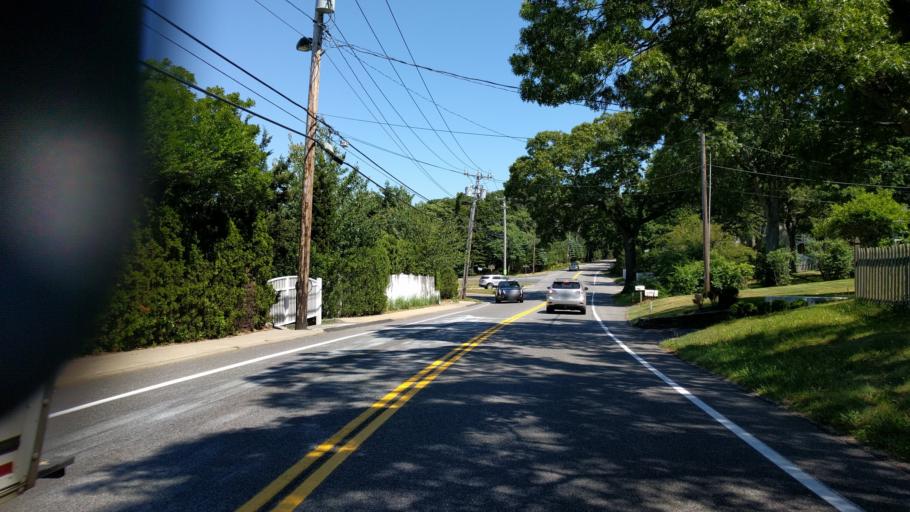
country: US
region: New York
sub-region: Suffolk County
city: Noyack
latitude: 40.9946
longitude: -72.3331
